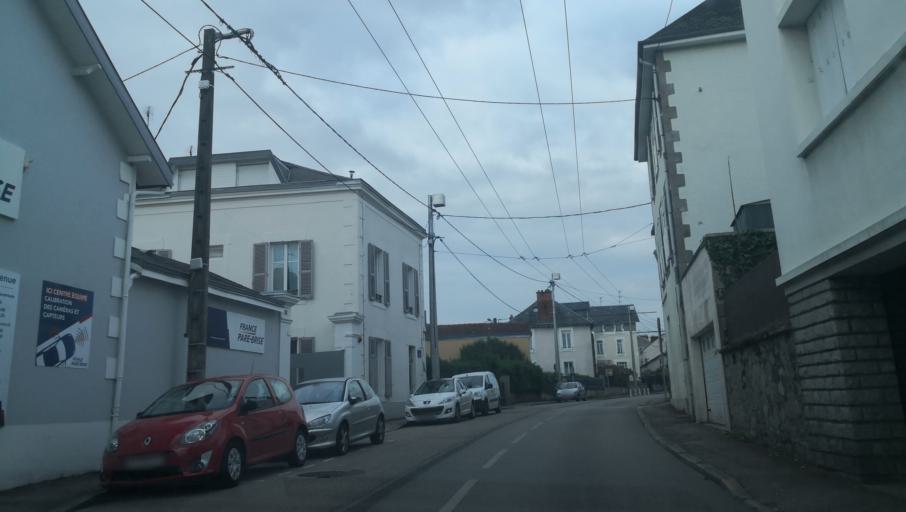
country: FR
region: Limousin
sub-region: Departement de la Haute-Vienne
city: Limoges
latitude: 45.8327
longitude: 1.2436
